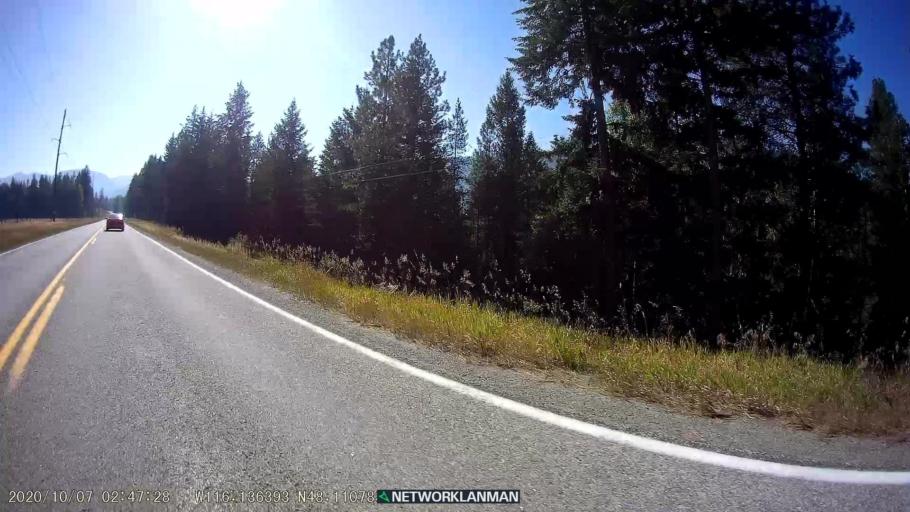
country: US
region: Idaho
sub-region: Bonner County
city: Ponderay
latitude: 48.1106
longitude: -116.1362
